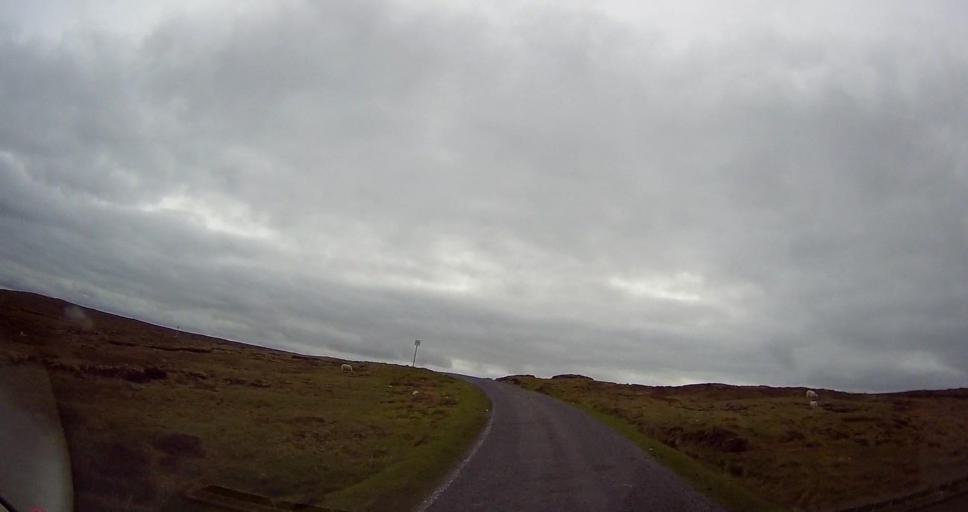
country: GB
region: Scotland
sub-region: Shetland Islands
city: Shetland
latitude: 60.5110
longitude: -1.1256
